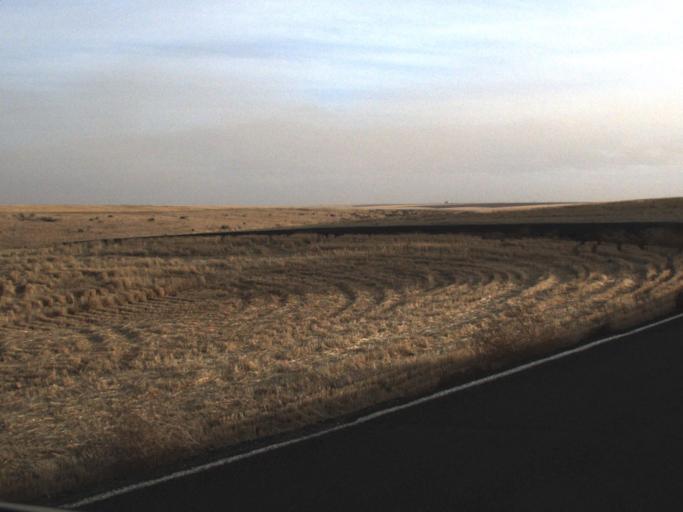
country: US
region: Washington
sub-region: Adams County
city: Ritzville
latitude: 47.2443
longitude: -118.6861
